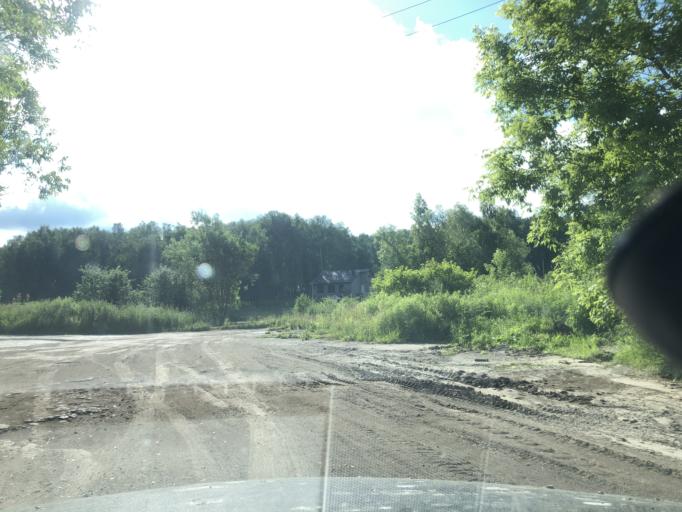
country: RU
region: Tula
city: Shvartsevskiy
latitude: 54.2519
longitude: 37.9281
